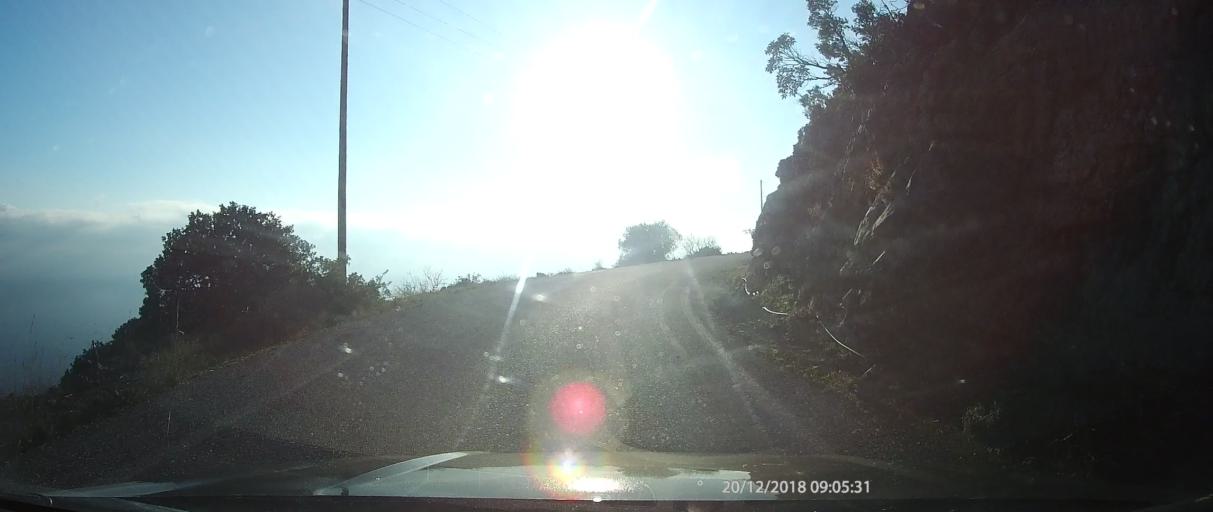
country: GR
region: Peloponnese
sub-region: Nomos Lakonias
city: Sykea
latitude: 36.9405
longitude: 22.9970
